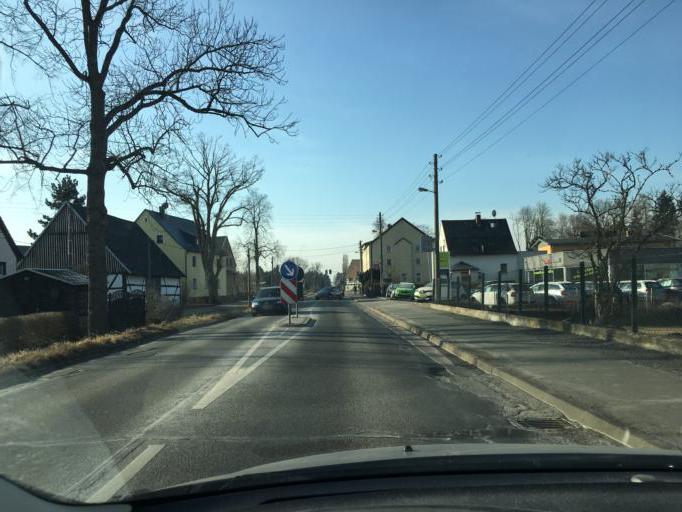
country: DE
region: Saxony
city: Glauchau
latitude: 50.8383
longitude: 12.5420
